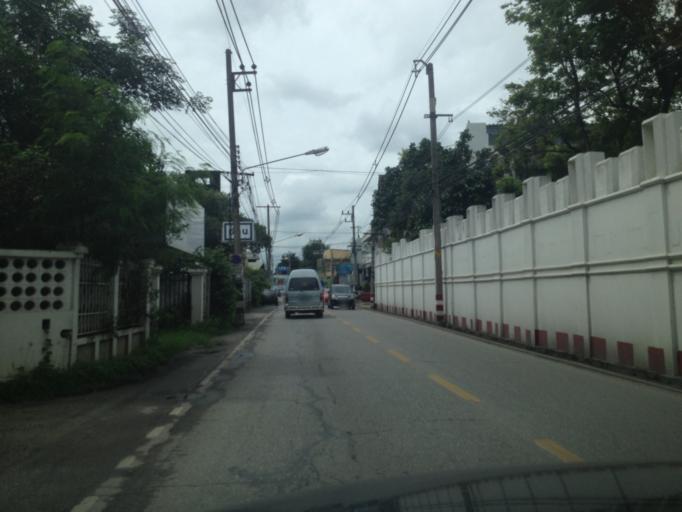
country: TH
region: Chiang Mai
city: Chiang Mai
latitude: 18.7801
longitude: 99.0071
